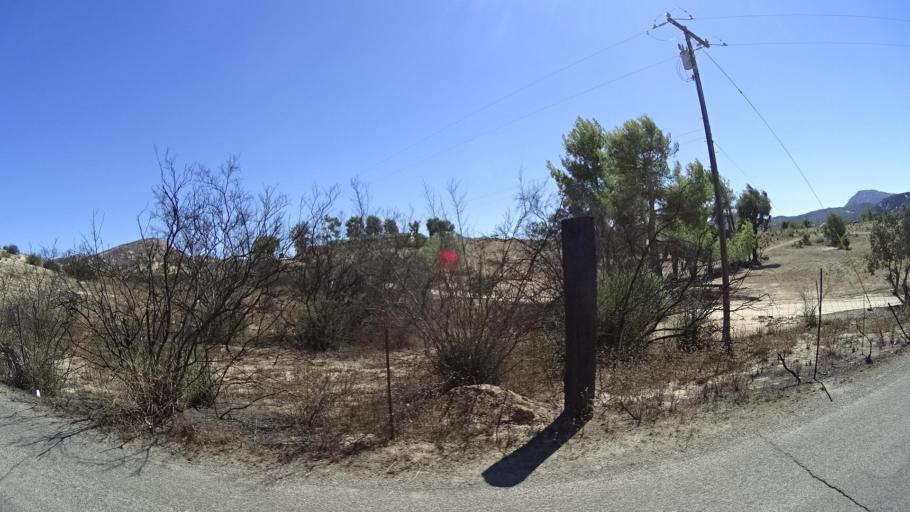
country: US
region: California
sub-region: San Diego County
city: Alpine
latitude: 32.7664
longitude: -116.7656
